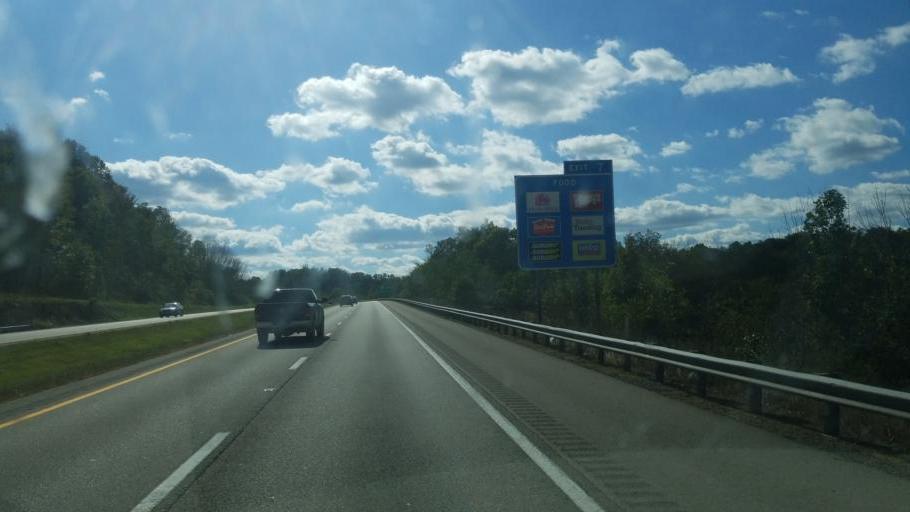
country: US
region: West Virginia
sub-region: Monongalia County
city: Cheat Lake
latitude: 39.6633
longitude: -79.8793
